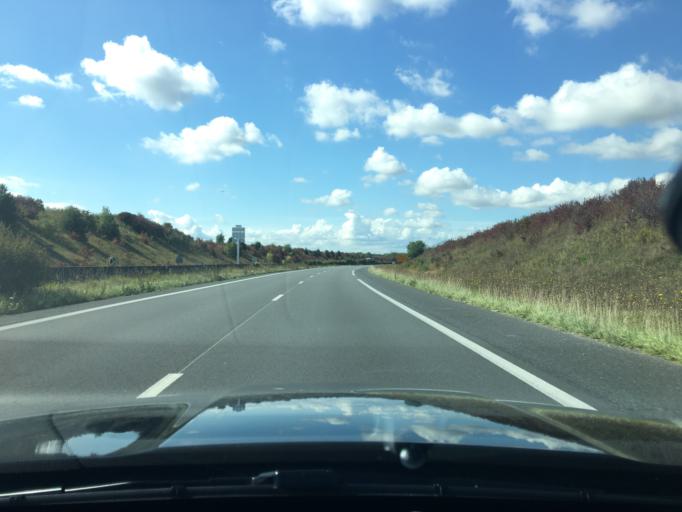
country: FR
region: Ile-de-France
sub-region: Departement du Val-d'Oise
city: Louvres
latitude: 49.0271
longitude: 2.5143
